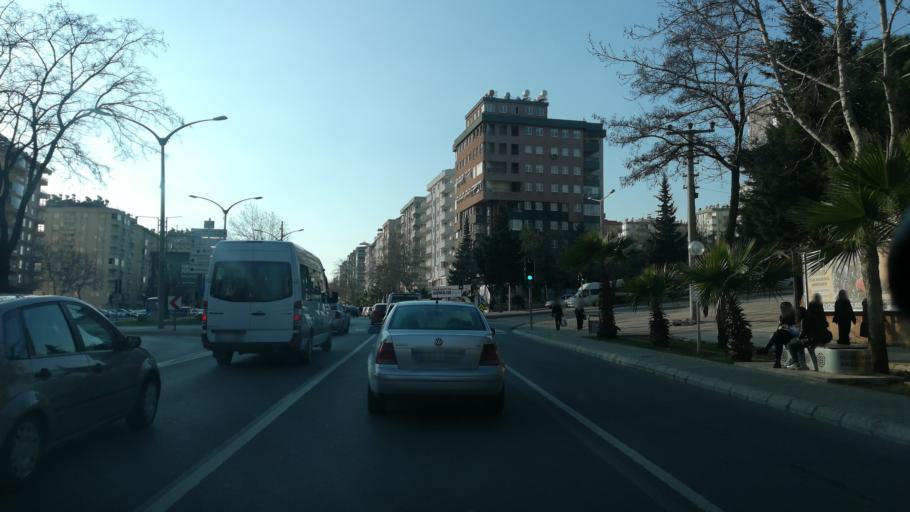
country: TR
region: Kahramanmaras
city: Kahramanmaras
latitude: 37.5884
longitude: 36.8878
